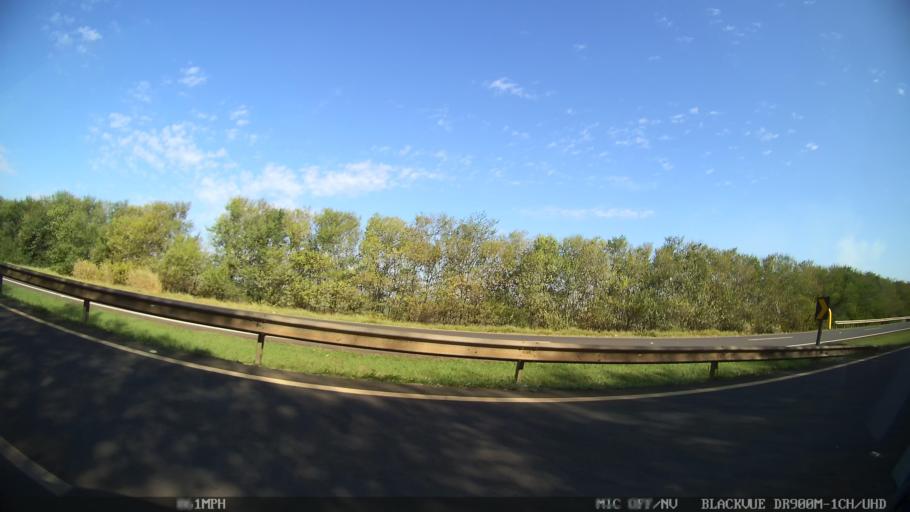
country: BR
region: Sao Paulo
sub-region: Iracemapolis
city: Iracemapolis
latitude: -22.6691
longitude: -47.5414
